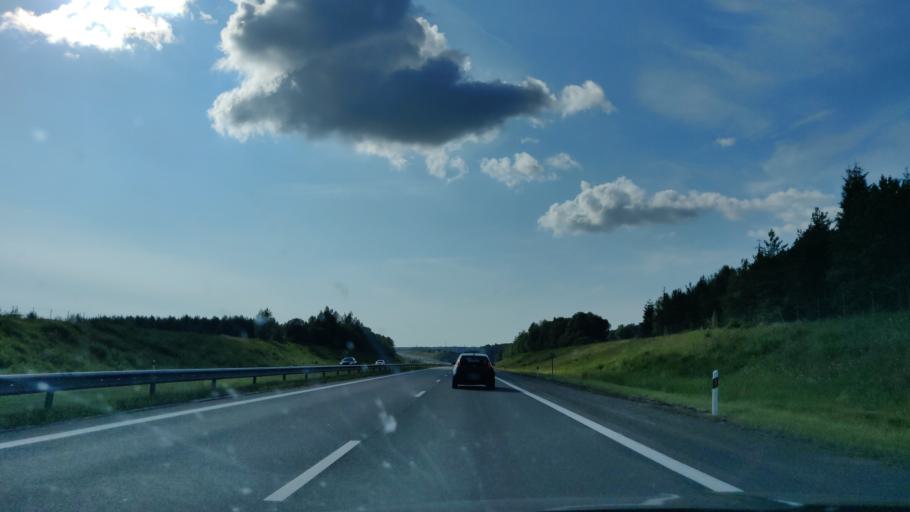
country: LT
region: Klaipedos apskritis
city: Gargzdai
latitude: 55.7234
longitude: 21.4283
